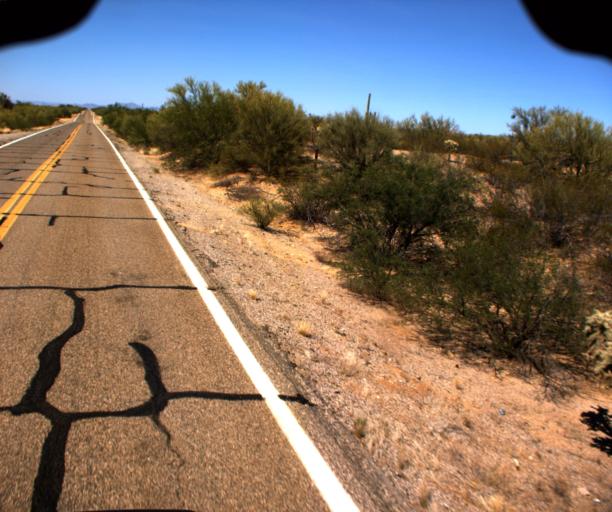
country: US
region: Arizona
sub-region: Pima County
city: Three Points
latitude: 31.9835
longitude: -111.3734
